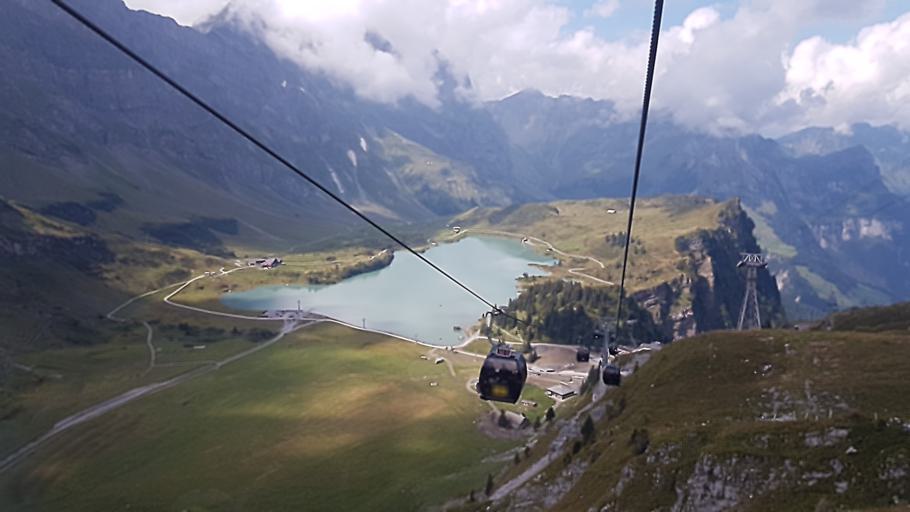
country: CH
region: Obwalden
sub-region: Obwalden
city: Engelberg
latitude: 46.7889
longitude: 8.4058
